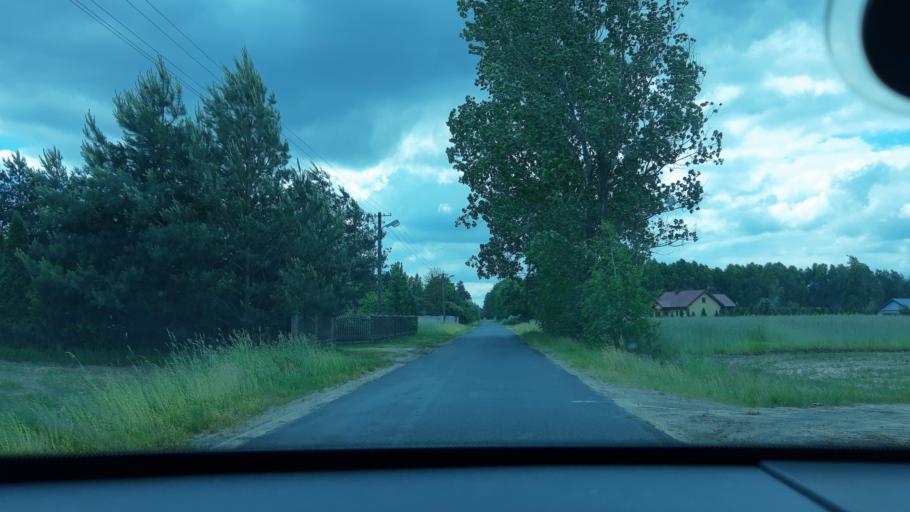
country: PL
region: Lodz Voivodeship
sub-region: Powiat zdunskowolski
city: Zapolice
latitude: 51.5219
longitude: 18.8436
